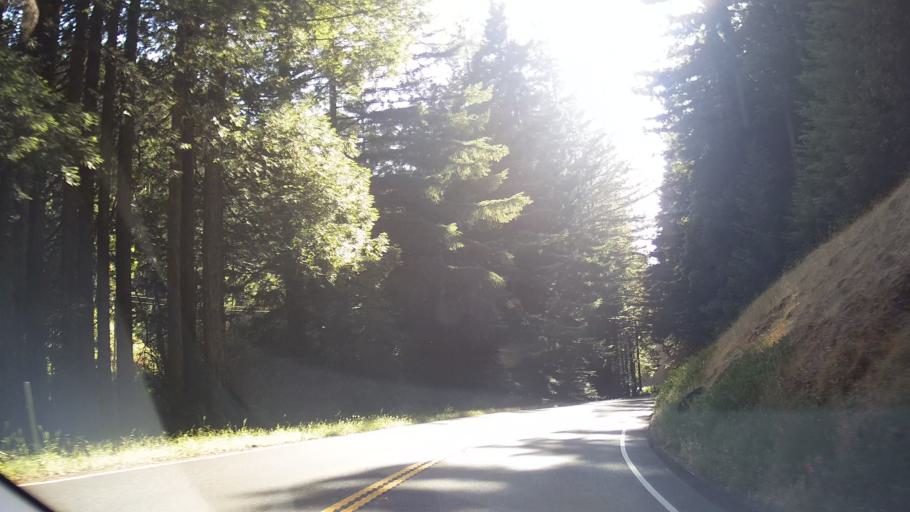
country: US
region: California
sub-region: Mendocino County
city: Brooktrails
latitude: 39.3486
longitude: -123.5835
